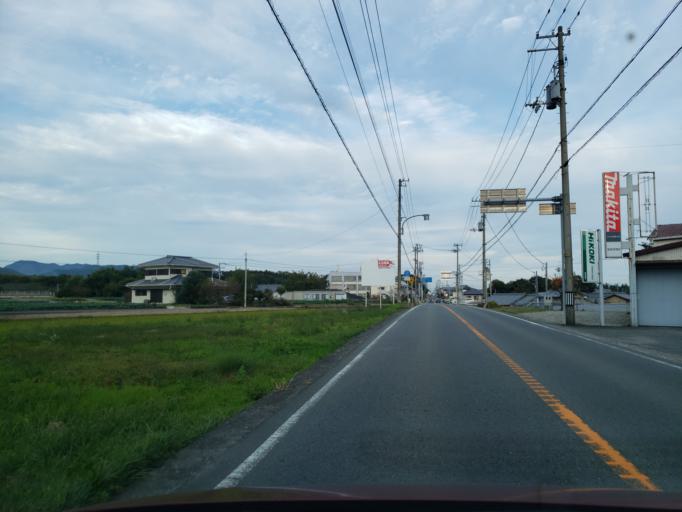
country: JP
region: Tokushima
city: Wakimachi
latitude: 34.0755
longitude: 134.2375
